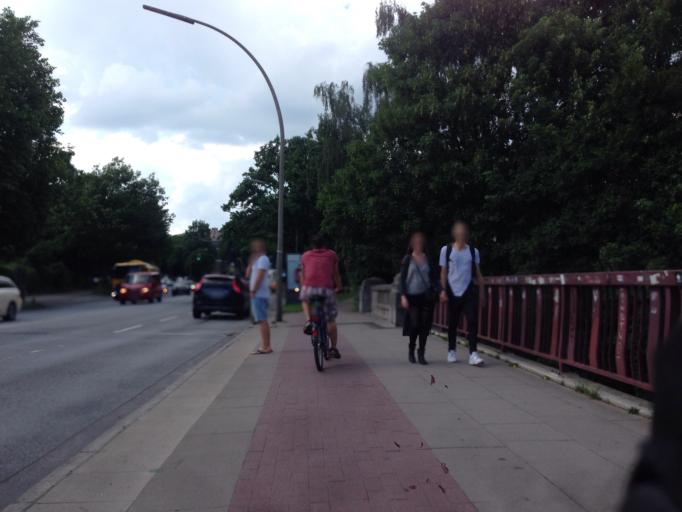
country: DE
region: Hamburg
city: Hamburg
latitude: 53.5876
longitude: 10.0169
